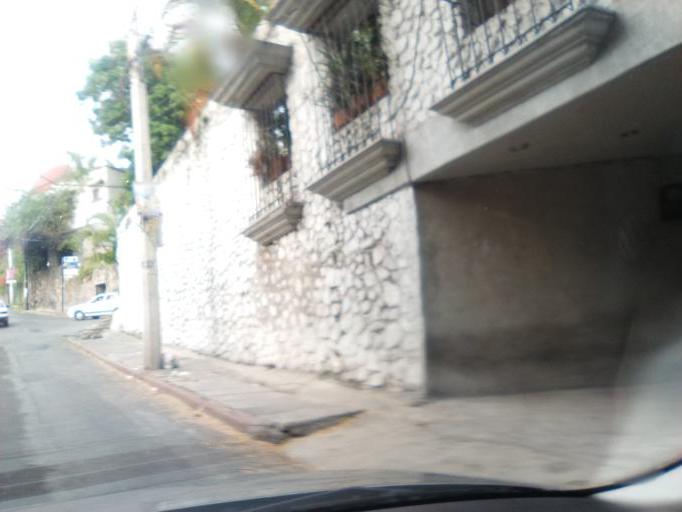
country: MX
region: Morelos
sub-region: Cuernavaca
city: Cuernavaca
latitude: 18.9124
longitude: -99.2293
